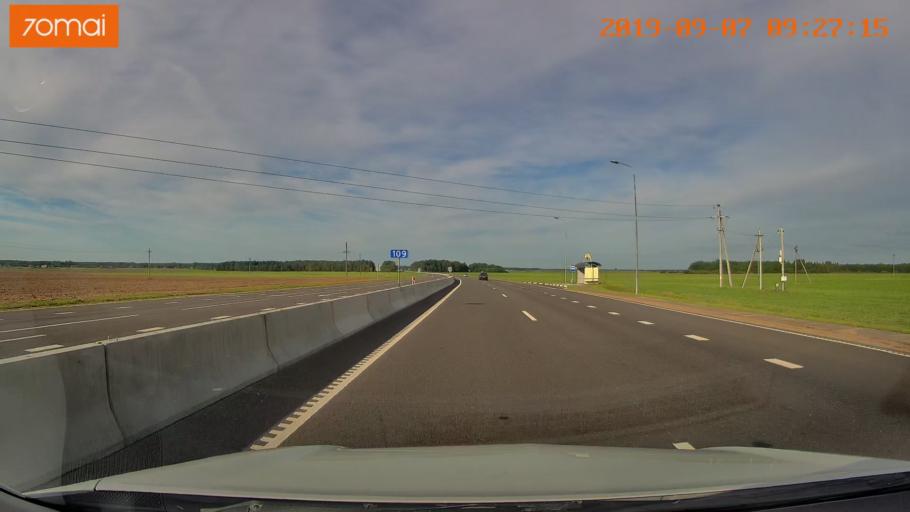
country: BY
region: Grodnenskaya
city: Lyubcha
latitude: 53.9120
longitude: 26.0826
